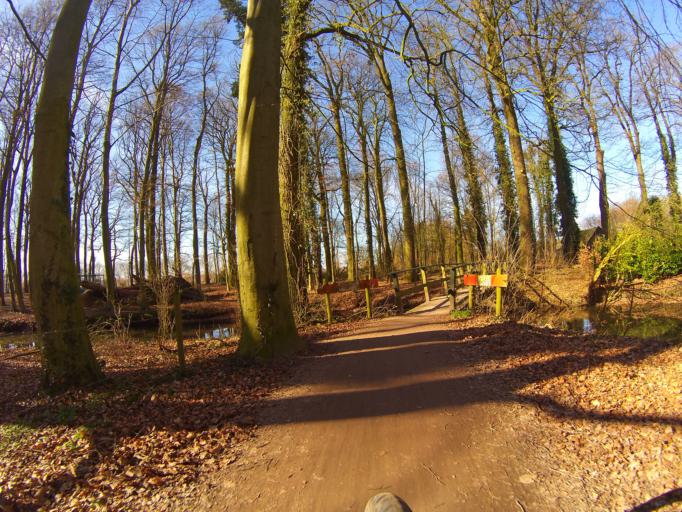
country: NL
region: Utrecht
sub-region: Gemeente Utrechtse Heuvelrug
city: Overberg
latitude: 52.0713
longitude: 5.4895
